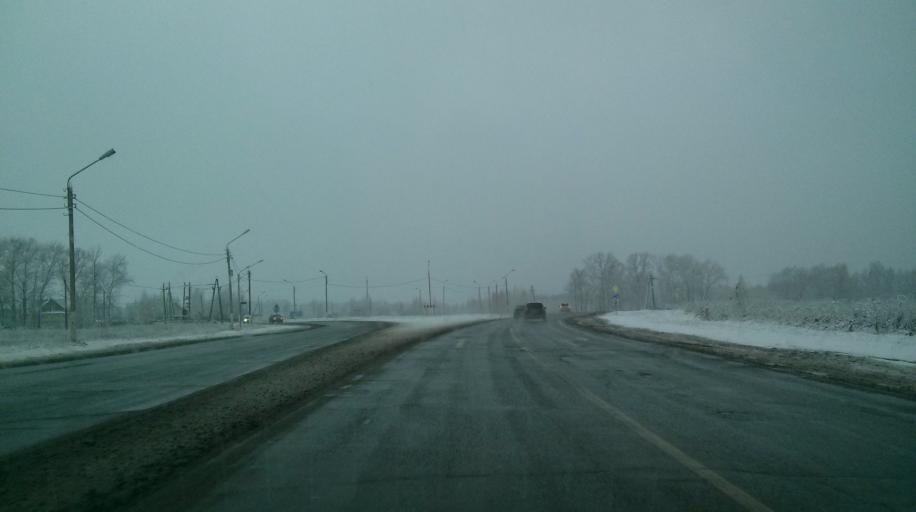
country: RU
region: Nizjnij Novgorod
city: Burevestnik
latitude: 56.1747
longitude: 43.7635
